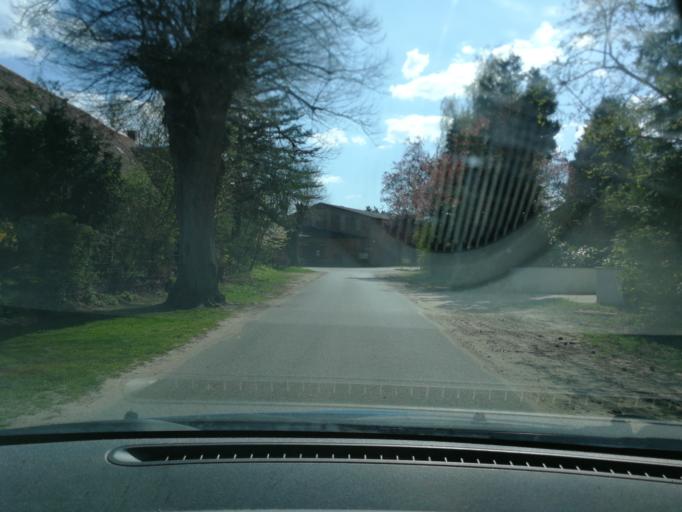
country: DE
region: Lower Saxony
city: Reinstorf
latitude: 53.2029
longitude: 10.5823
